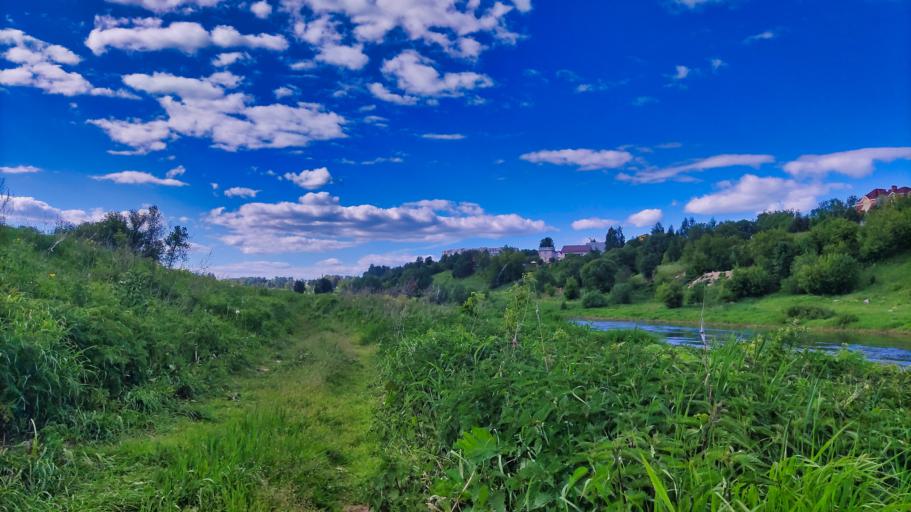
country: RU
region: Tverskaya
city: Rzhev
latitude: 56.2501
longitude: 34.3485
